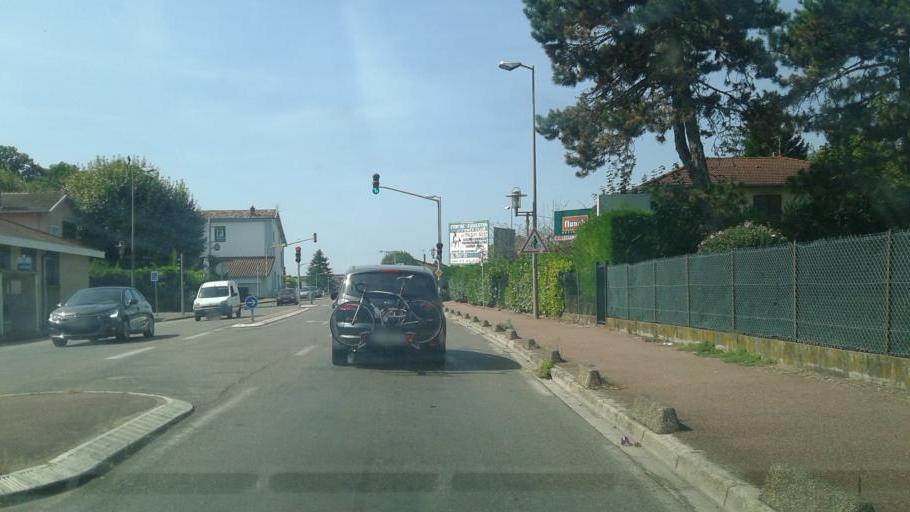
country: FR
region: Rhone-Alpes
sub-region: Departement de l'Ain
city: La Boisse
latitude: 45.8450
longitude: 5.0355
